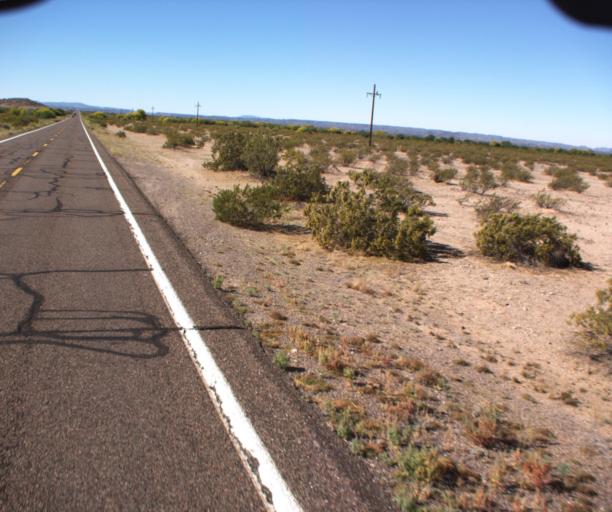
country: US
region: Arizona
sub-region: Maricopa County
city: Gila Bend
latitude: 32.7105
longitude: -112.8443
